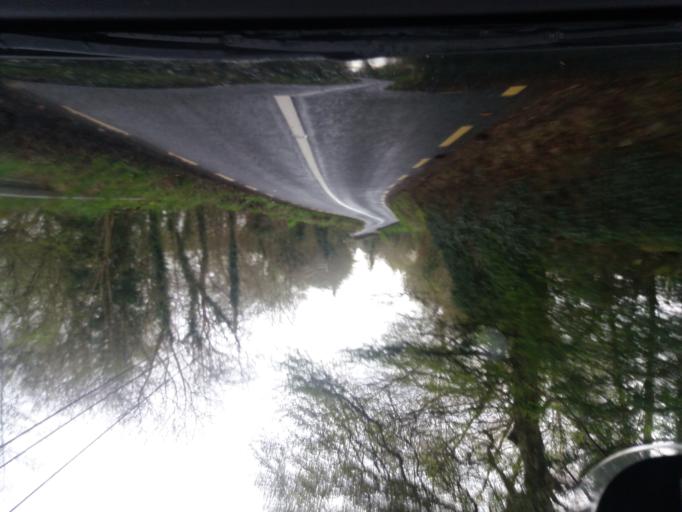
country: IE
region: Ulster
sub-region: An Cabhan
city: Ballyconnell
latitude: 54.1374
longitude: -7.6966
